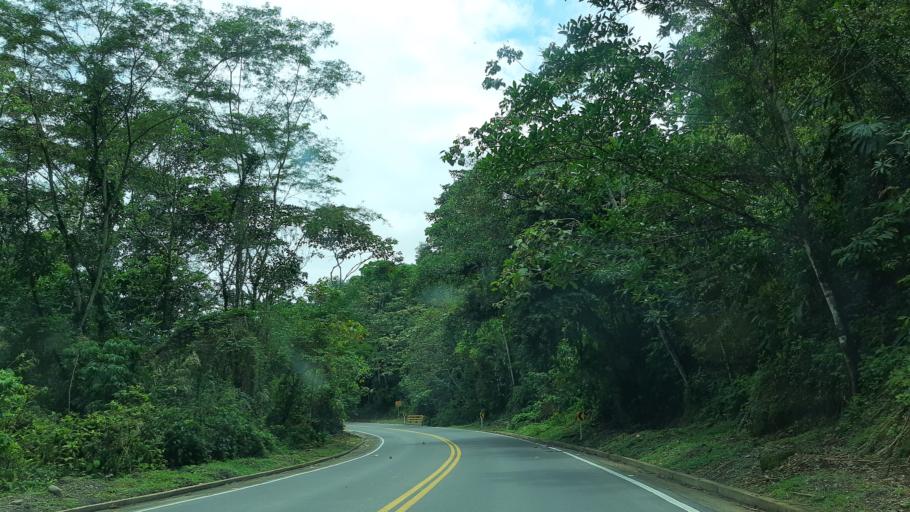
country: CO
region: Boyaca
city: San Luis de Gaceno
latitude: 4.8338
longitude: -73.1362
